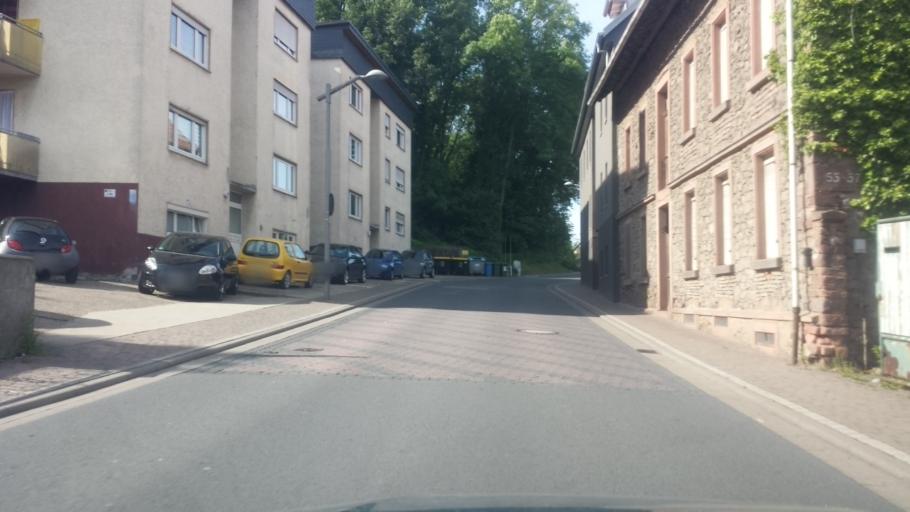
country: DE
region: Hesse
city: Ober-Ramstadt
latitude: 49.8240
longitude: 8.7481
